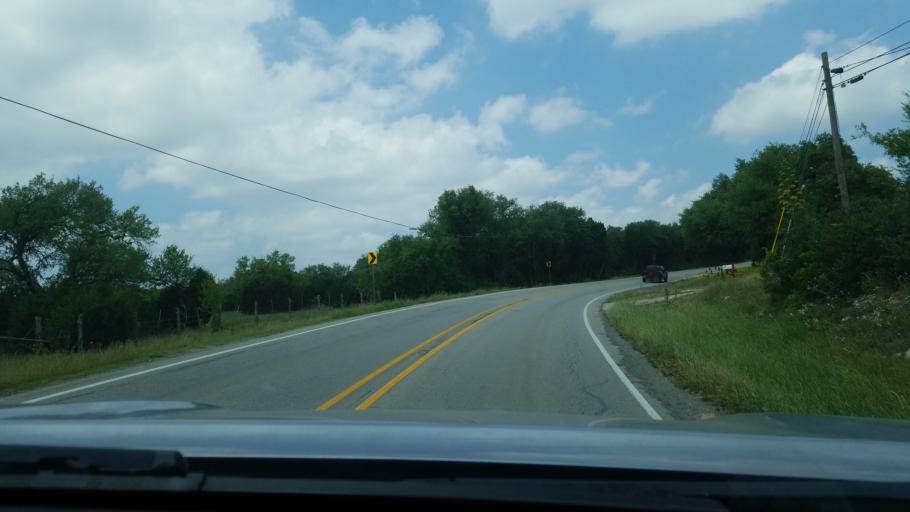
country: US
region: Texas
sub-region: Hays County
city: Dripping Springs
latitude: 30.1543
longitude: -98.0670
